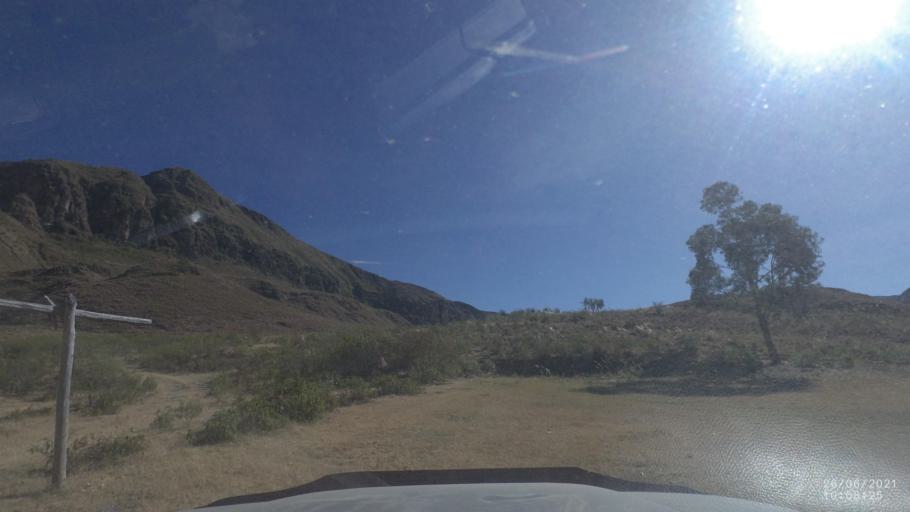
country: BO
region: Cochabamba
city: Mizque
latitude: -17.9193
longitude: -65.6251
